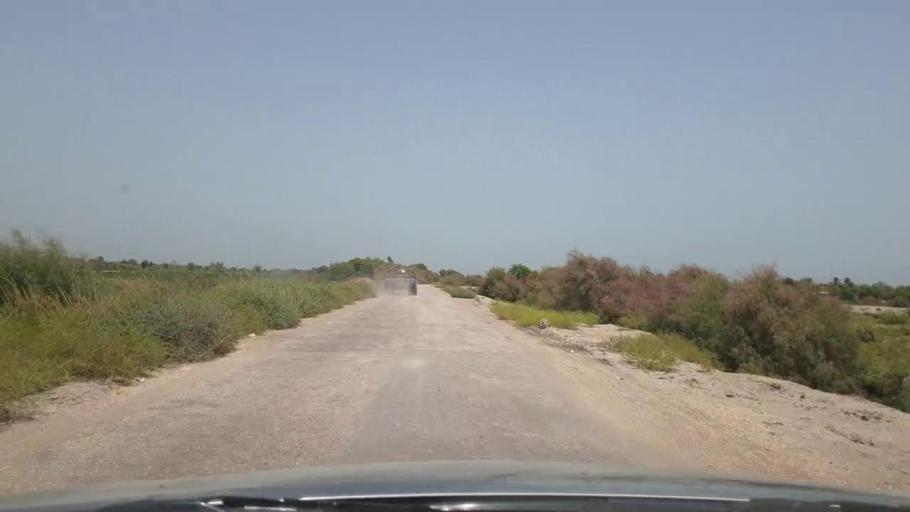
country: PK
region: Sindh
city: Pano Aqil
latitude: 27.8710
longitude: 69.1661
